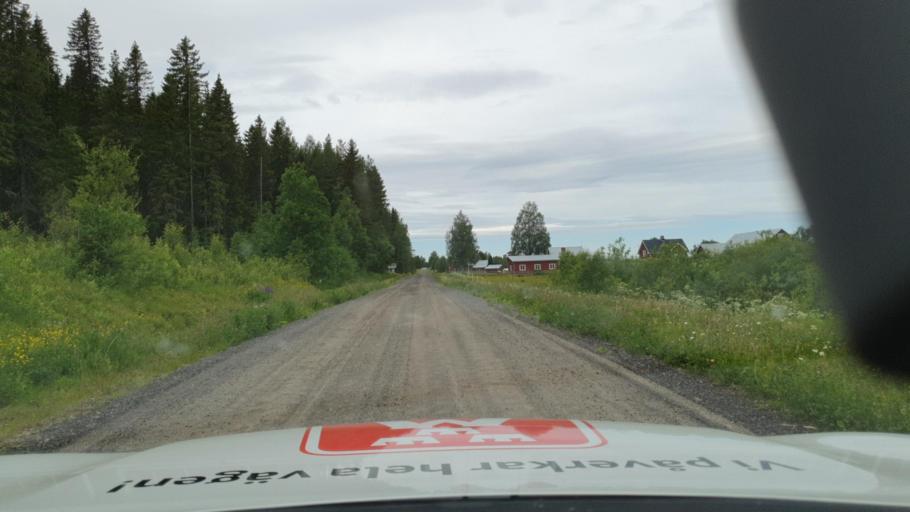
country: SE
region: Vaesterbotten
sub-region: Skelleftea Kommun
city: Burtraesk
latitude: 64.3906
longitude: 20.6076
